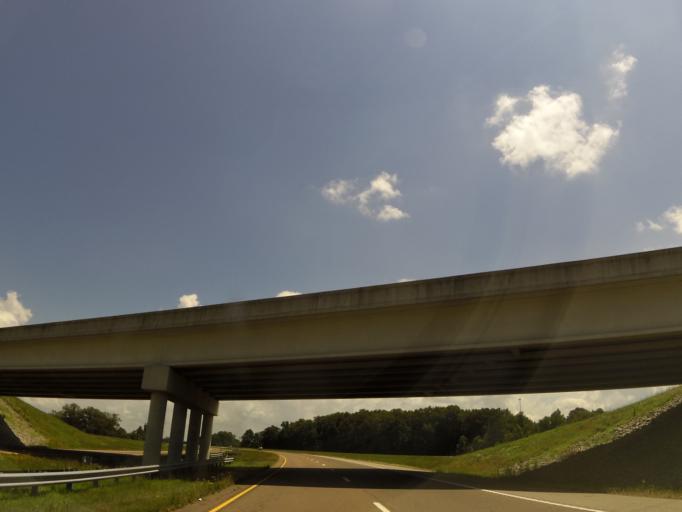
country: US
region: Tennessee
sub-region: Crockett County
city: Alamo
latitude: 35.7970
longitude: -89.1597
